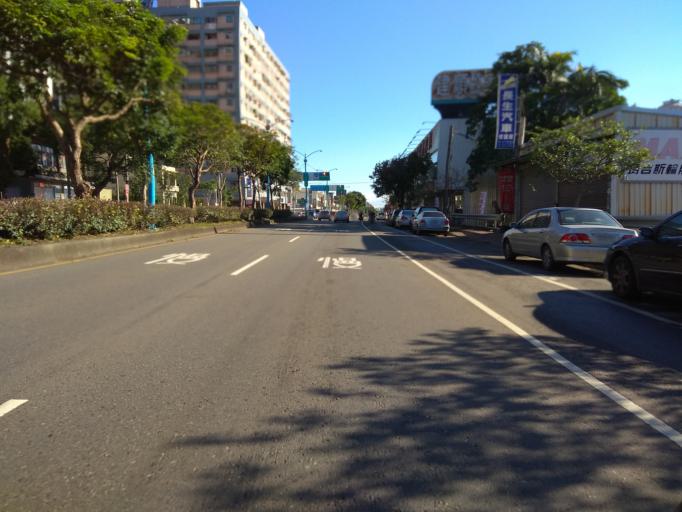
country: TW
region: Taiwan
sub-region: Hsinchu
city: Zhubei
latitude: 24.9033
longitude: 121.1266
